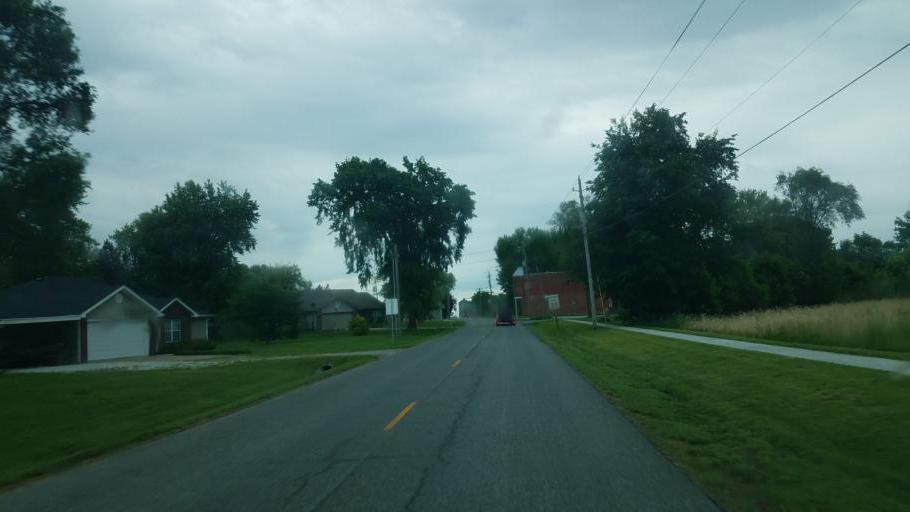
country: US
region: Missouri
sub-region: Moniteau County
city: California
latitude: 38.8142
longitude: -92.5922
